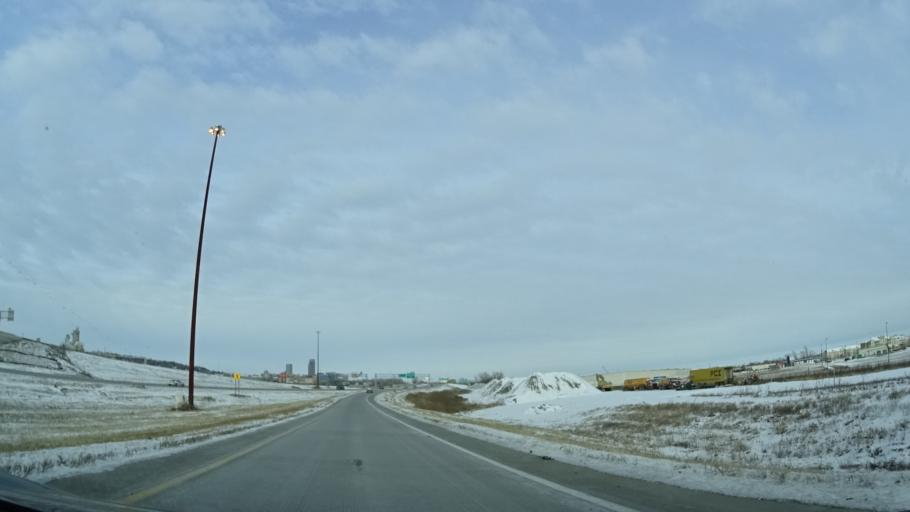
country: US
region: Iowa
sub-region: Pottawattamie County
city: Council Bluffs
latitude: 41.2359
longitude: -95.8979
